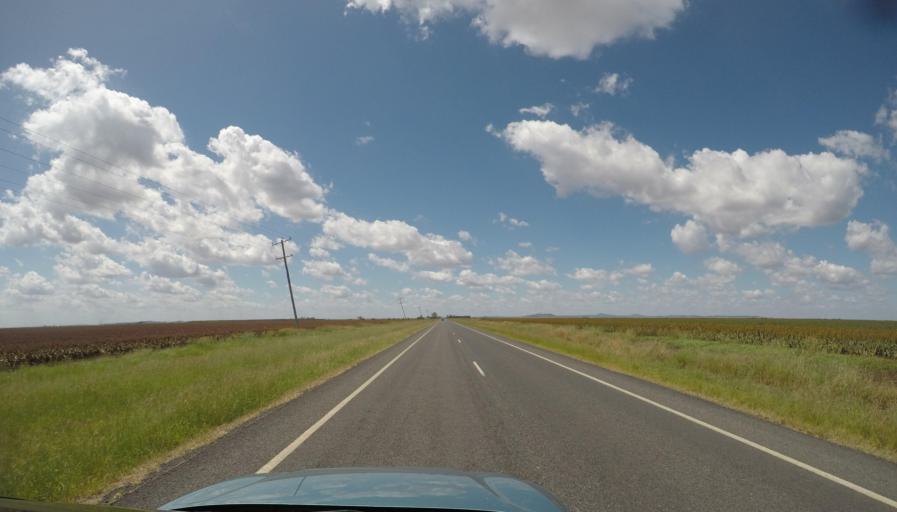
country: AU
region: Queensland
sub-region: Toowoomba
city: Oakey
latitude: -27.5169
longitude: 151.4055
